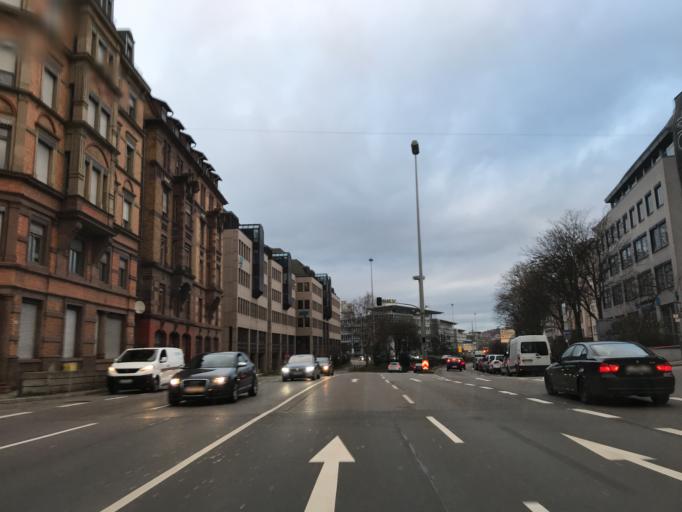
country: DE
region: Baden-Wuerttemberg
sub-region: Regierungsbezirk Stuttgart
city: Stuttgart
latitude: 48.7661
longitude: 9.1722
